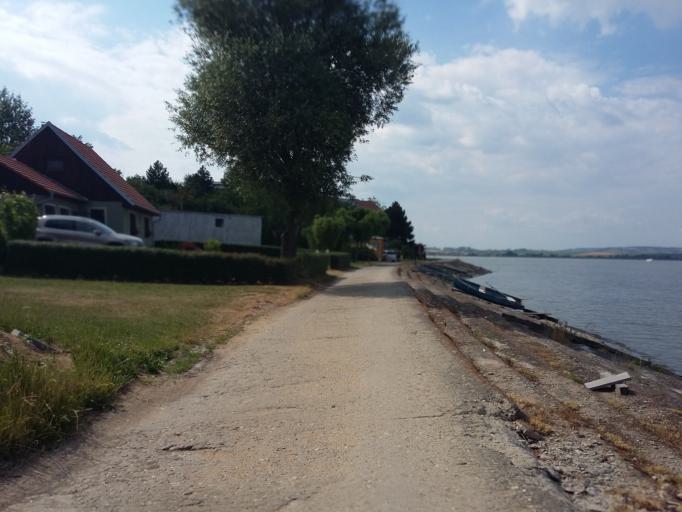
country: CZ
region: South Moravian
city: Sakvice
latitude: 48.8813
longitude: 16.6736
